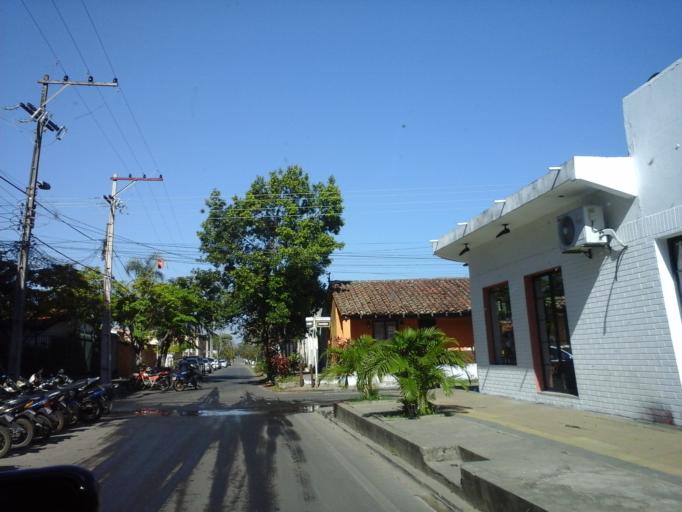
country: PY
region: Neembucu
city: Pilar
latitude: -26.8571
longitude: -58.3077
